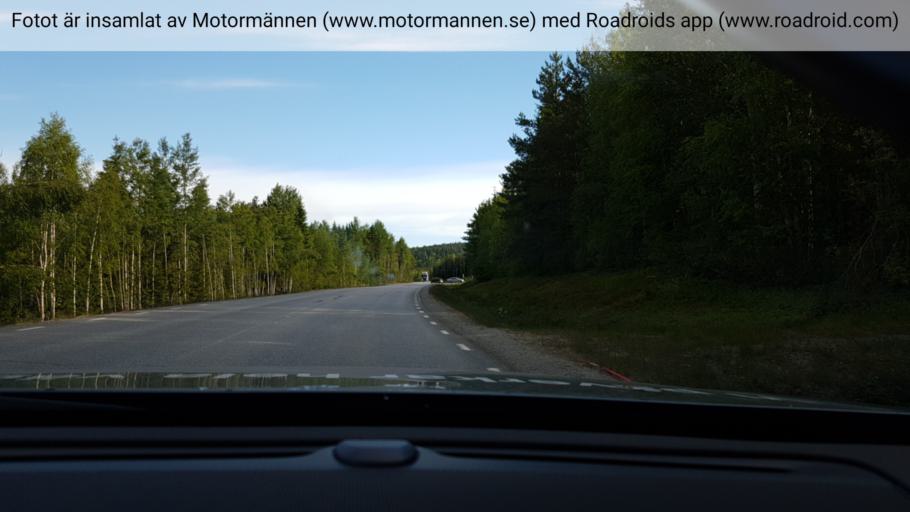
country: SE
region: Vaesterbotten
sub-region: Vannas Kommun
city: Vaennaes
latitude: 63.9336
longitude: 19.7710
